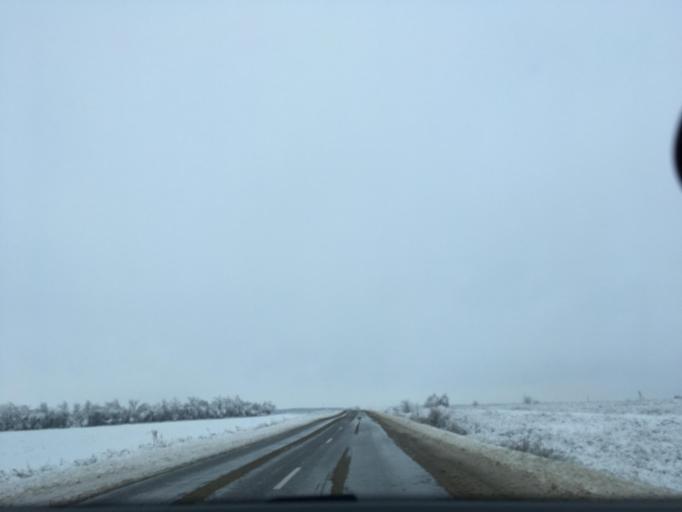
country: RU
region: Voronezj
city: Ol'khovatka
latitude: 50.1290
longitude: 39.1919
